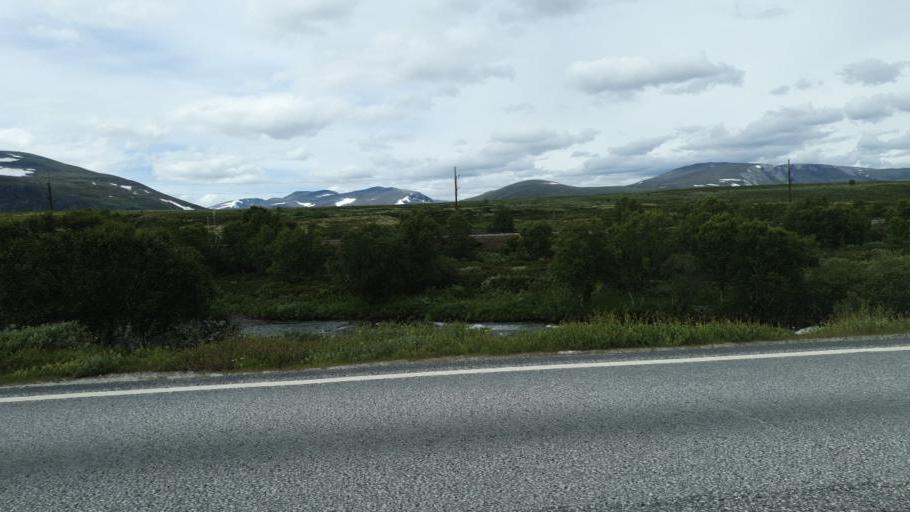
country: NO
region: Sor-Trondelag
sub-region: Oppdal
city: Oppdal
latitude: 62.2648
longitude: 9.5682
